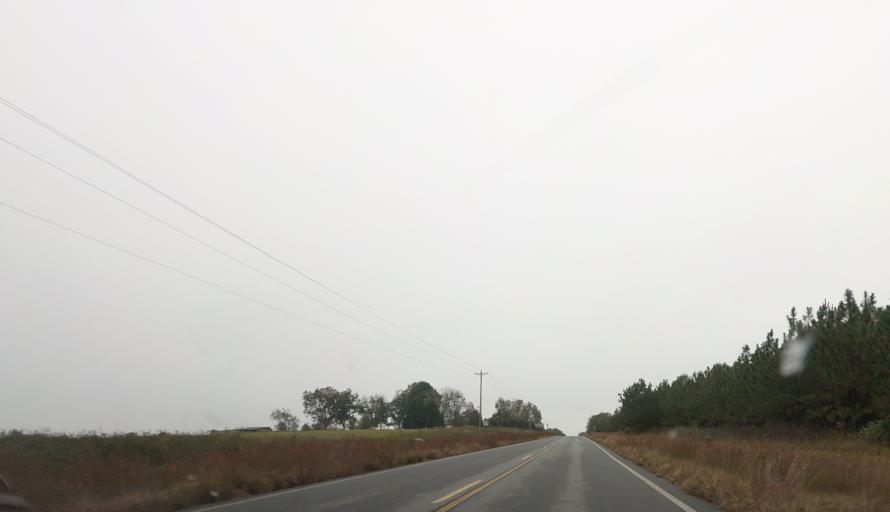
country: US
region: Georgia
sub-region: Marion County
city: Buena Vista
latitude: 32.4022
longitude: -84.4137
